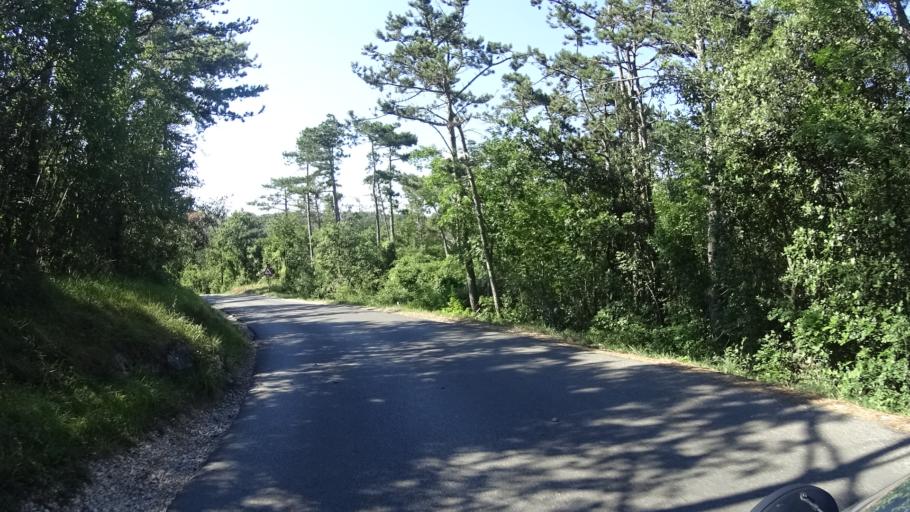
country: HR
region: Istarska
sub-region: Grad Labin
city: Labin
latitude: 45.0633
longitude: 14.1268
